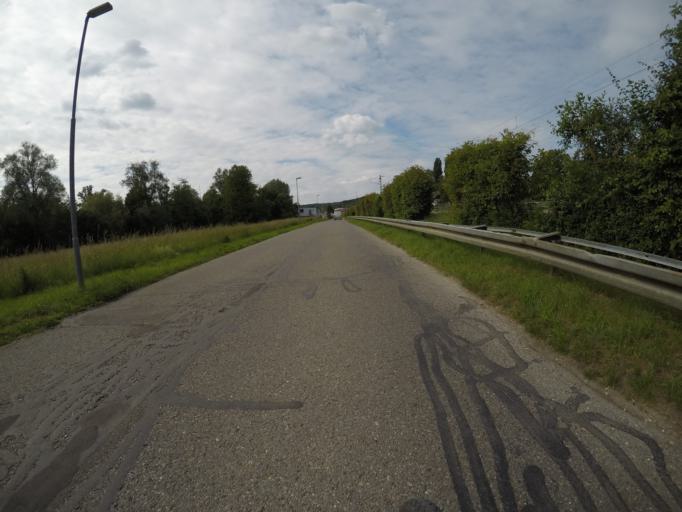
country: DE
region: Baden-Wuerttemberg
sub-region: Karlsruhe Region
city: Joehlingen
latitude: 48.9973
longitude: 8.5385
